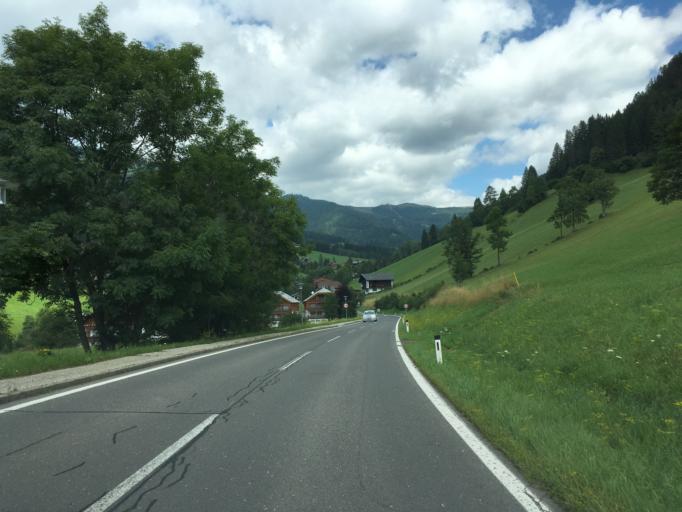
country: AT
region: Carinthia
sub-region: Politischer Bezirk Spittal an der Drau
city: Kleinkirchheim
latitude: 46.8175
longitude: 13.7756
